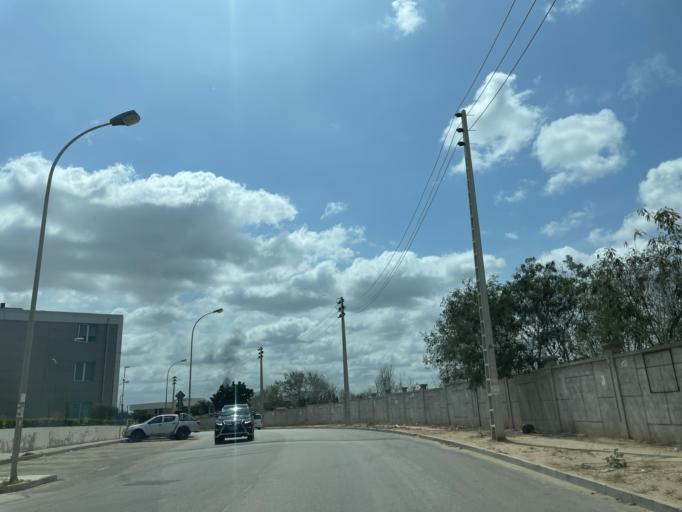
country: AO
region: Luanda
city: Luanda
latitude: -8.9308
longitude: 13.1878
